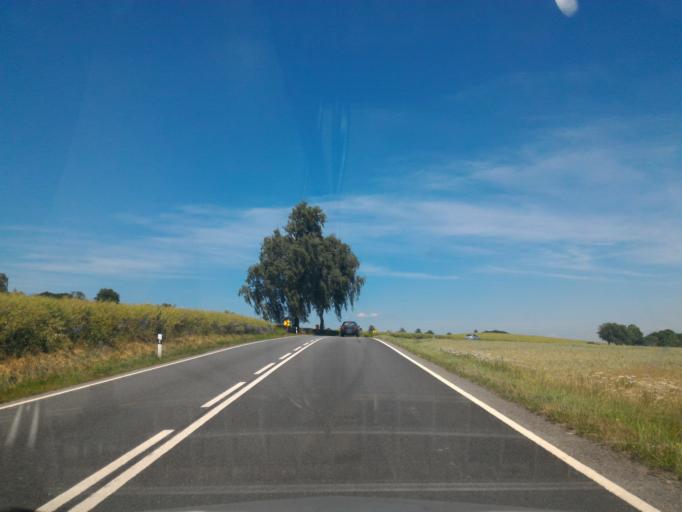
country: CZ
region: Vysocina
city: Dolni Cerekev
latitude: 49.3435
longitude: 15.4842
